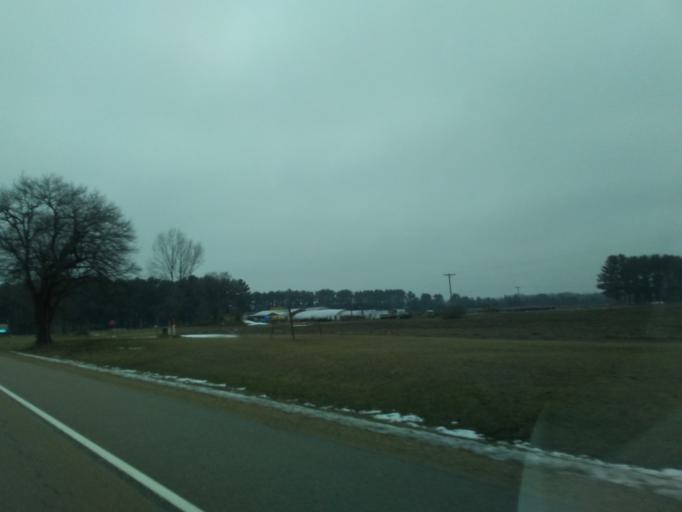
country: US
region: Wisconsin
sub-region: Sauk County
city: Spring Green
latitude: 43.1617
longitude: -89.9496
